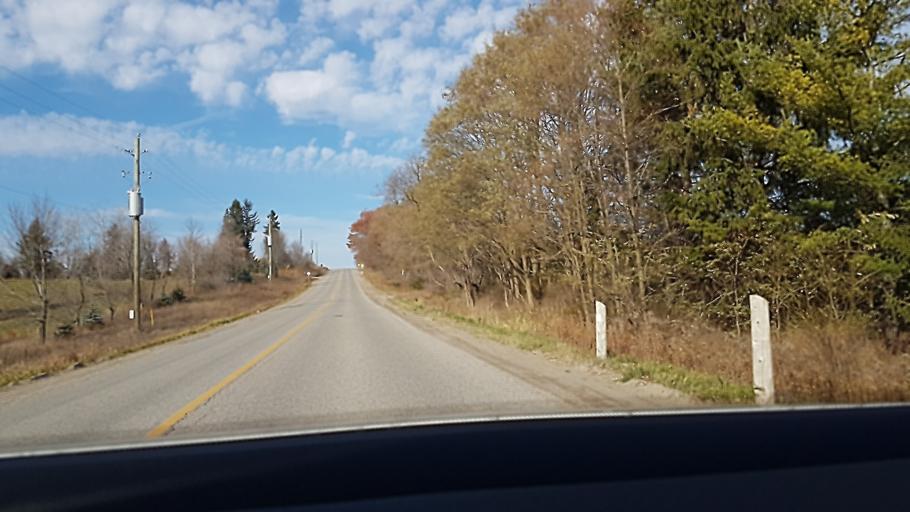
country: CA
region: Ontario
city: Bradford West Gwillimbury
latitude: 44.0510
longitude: -79.7738
